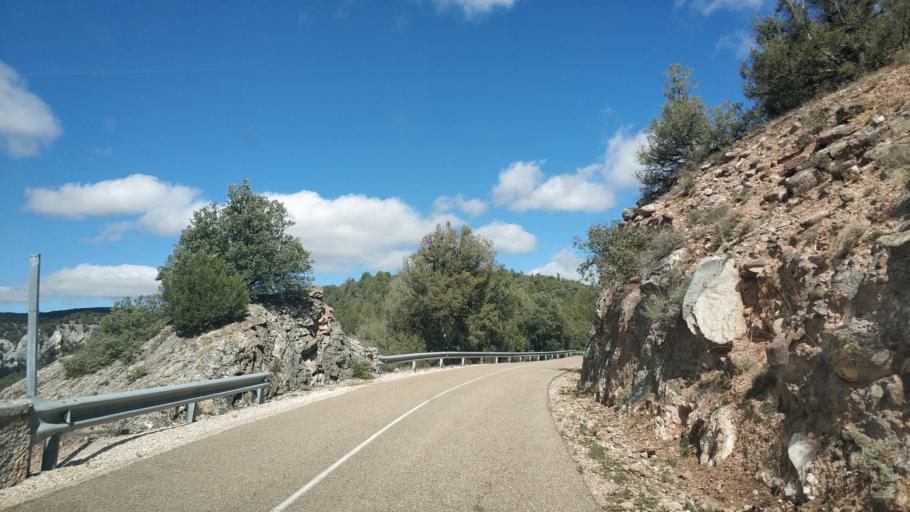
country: ES
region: Castille and Leon
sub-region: Provincia de Burgos
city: Retuerta
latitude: 42.0430
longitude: -3.4763
